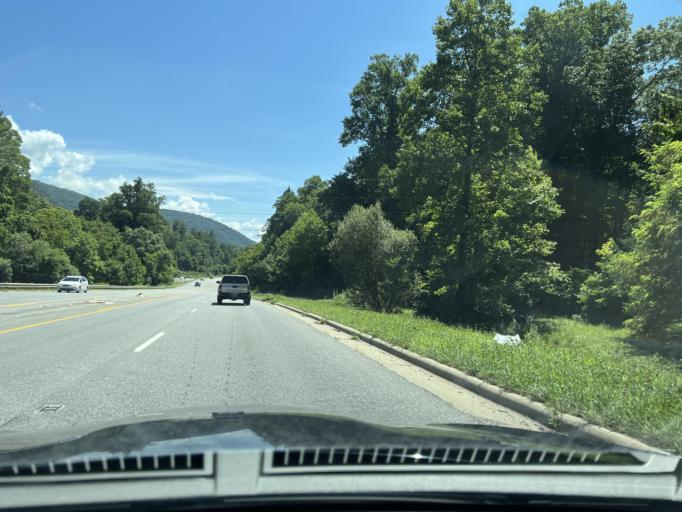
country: US
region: North Carolina
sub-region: Buncombe County
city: Fairview
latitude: 35.5457
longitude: -82.4513
